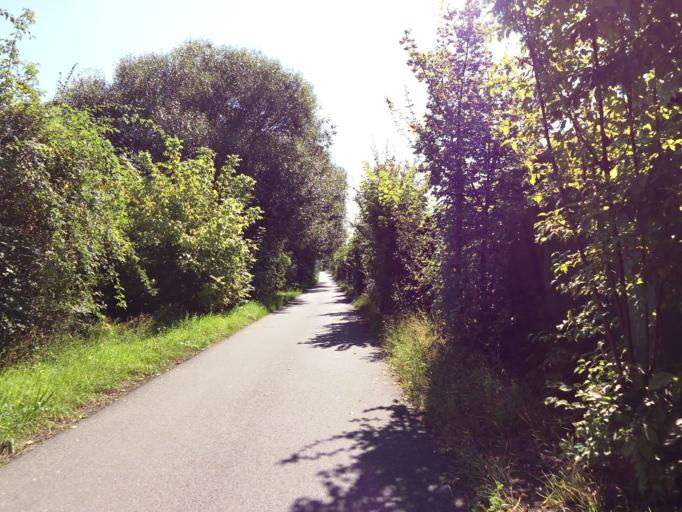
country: DE
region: Rheinland-Pfalz
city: Mainz
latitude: 49.9843
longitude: 8.3028
